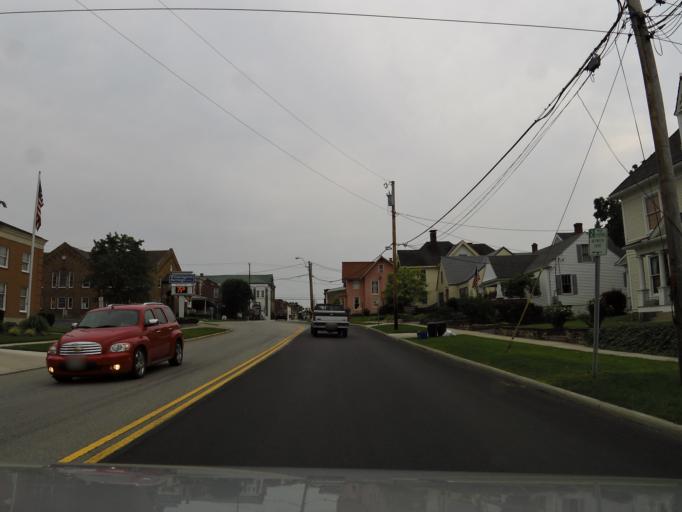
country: US
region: Ohio
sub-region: Clinton County
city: Wilmington
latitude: 39.4483
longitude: -83.8285
